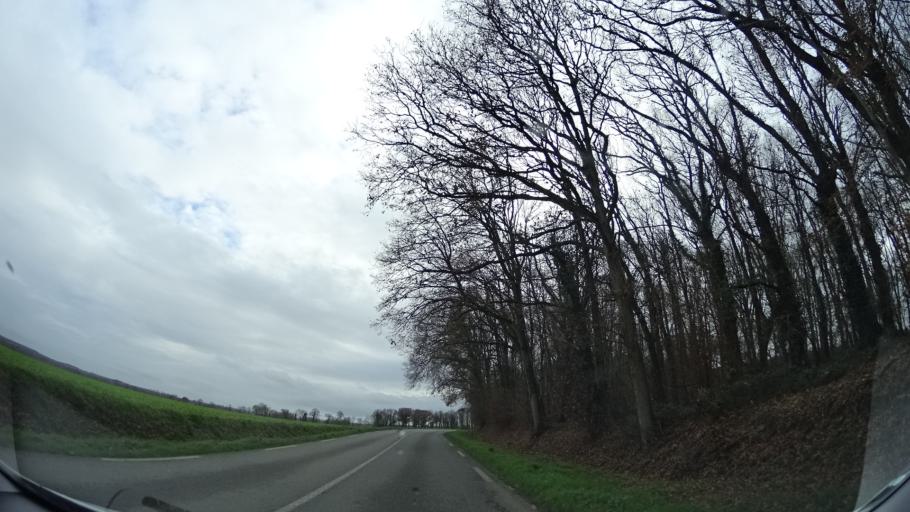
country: FR
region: Brittany
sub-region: Departement des Cotes-d'Armor
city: Evran
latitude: 48.3573
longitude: -1.9690
